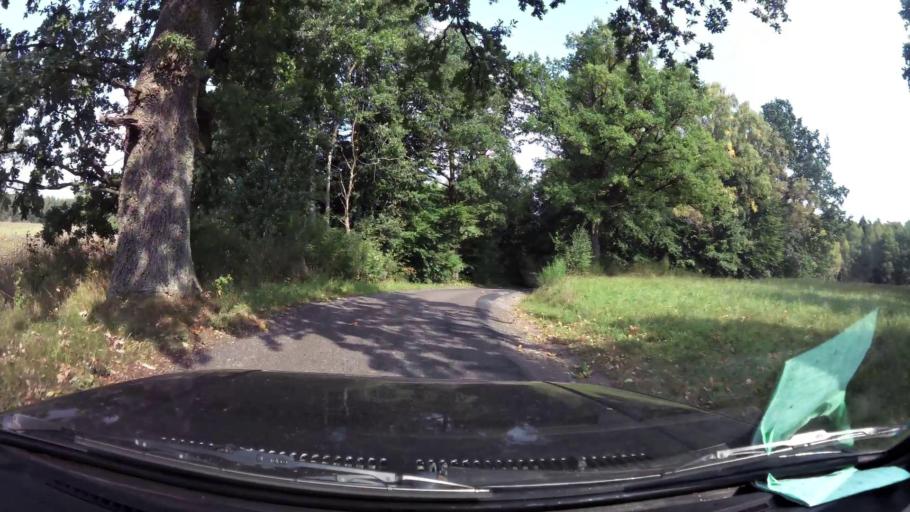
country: PL
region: West Pomeranian Voivodeship
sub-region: Powiat koszalinski
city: Polanow
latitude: 54.1288
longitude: 16.5194
